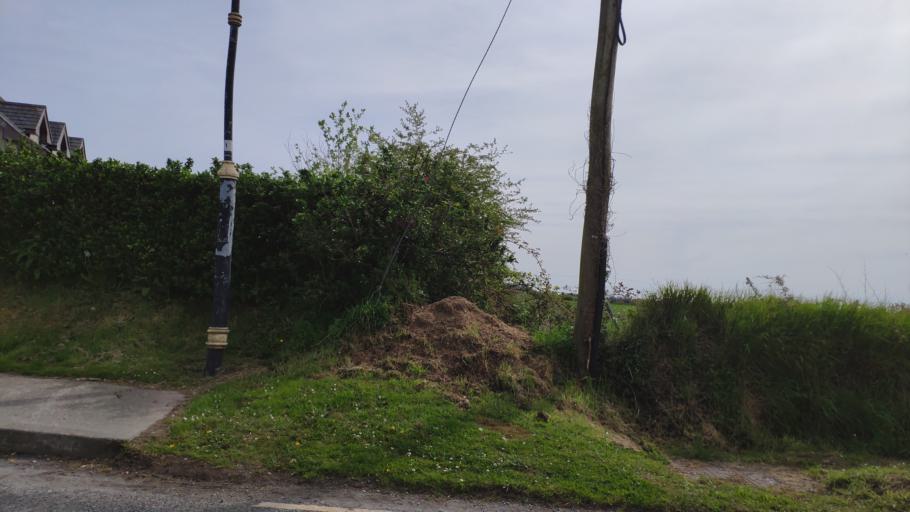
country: IE
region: Munster
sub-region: County Cork
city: Blarney
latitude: 51.9783
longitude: -8.5134
